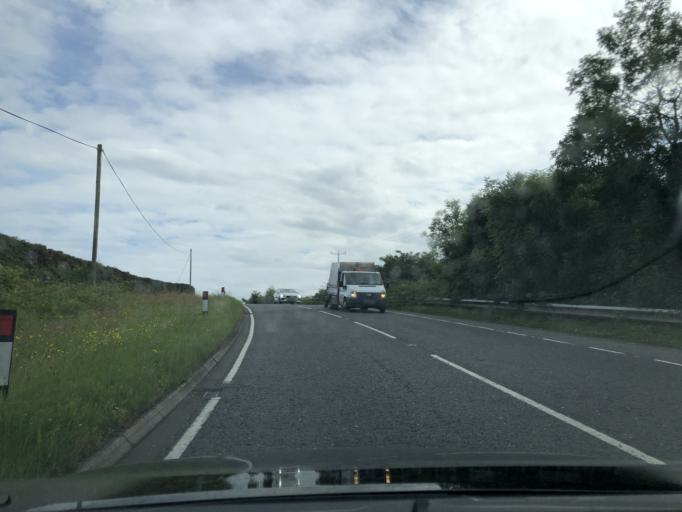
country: GB
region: Northern Ireland
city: Ballynahinch
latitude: 54.3583
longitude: -5.8577
